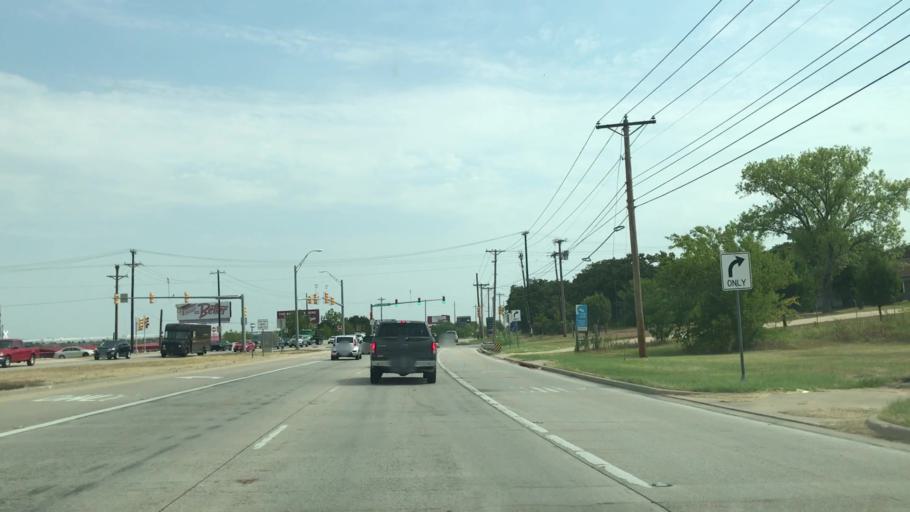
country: US
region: Texas
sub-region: Tarrant County
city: Keller
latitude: 32.9555
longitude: -97.2542
